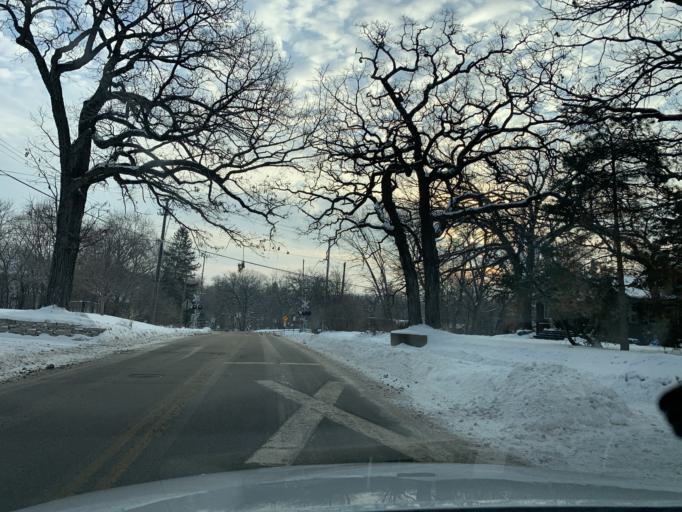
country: US
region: Minnesota
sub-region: Hennepin County
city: Saint Louis Park
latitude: 44.9224
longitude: -93.3550
